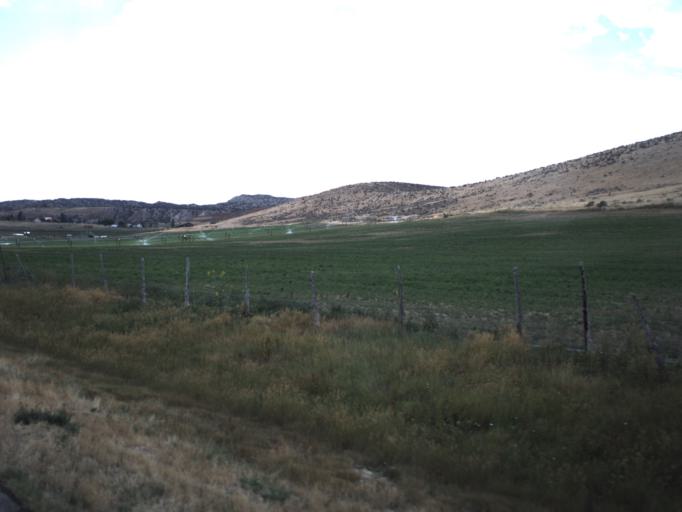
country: US
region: Utah
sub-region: Sanpete County
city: Gunnison
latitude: 39.1452
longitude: -111.7096
